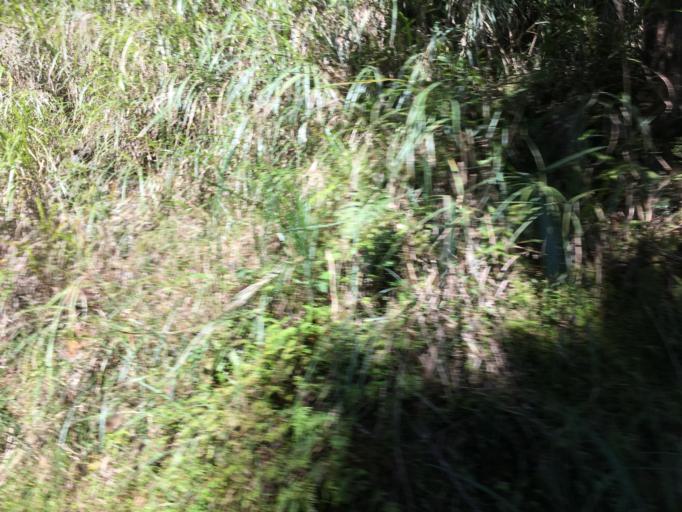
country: TW
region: Taiwan
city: Daxi
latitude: 24.6072
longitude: 121.4596
